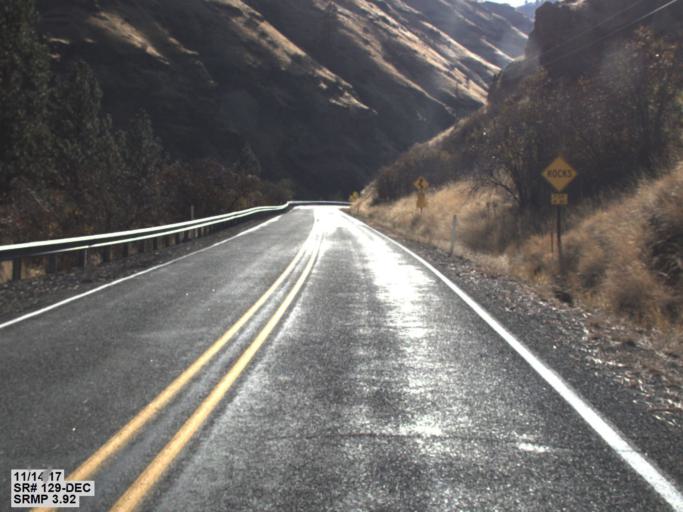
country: US
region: Washington
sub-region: Asotin County
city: Asotin
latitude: 46.0358
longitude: -117.2553
